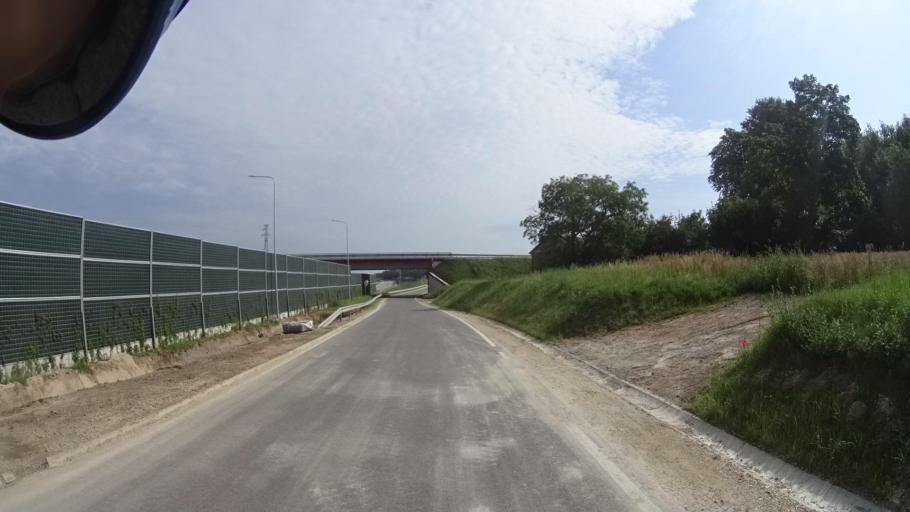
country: PL
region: Masovian Voivodeship
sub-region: Powiat piaseczynski
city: Tarczyn
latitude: 51.9560
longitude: 20.8506
